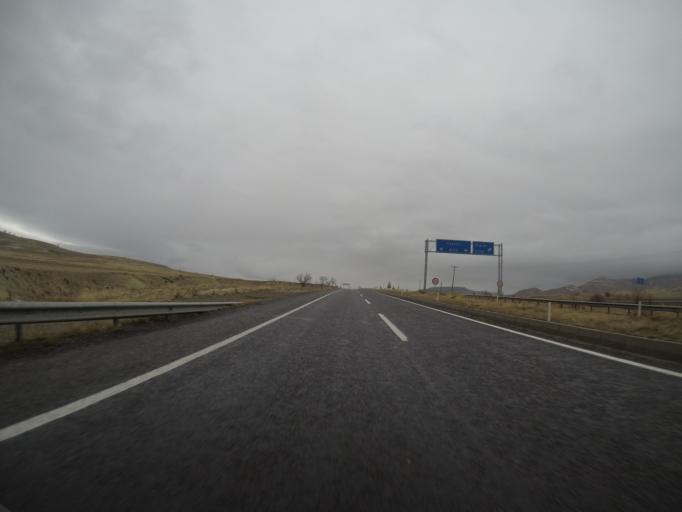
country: TR
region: Nevsehir
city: Avanos
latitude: 38.7134
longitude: 34.9286
